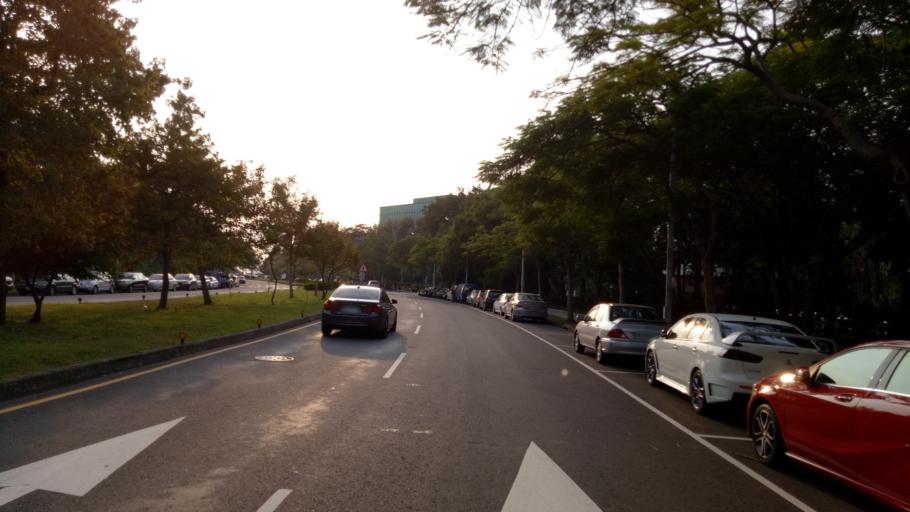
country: TW
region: Taiwan
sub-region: Hsinchu
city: Hsinchu
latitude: 24.7683
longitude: 121.0186
